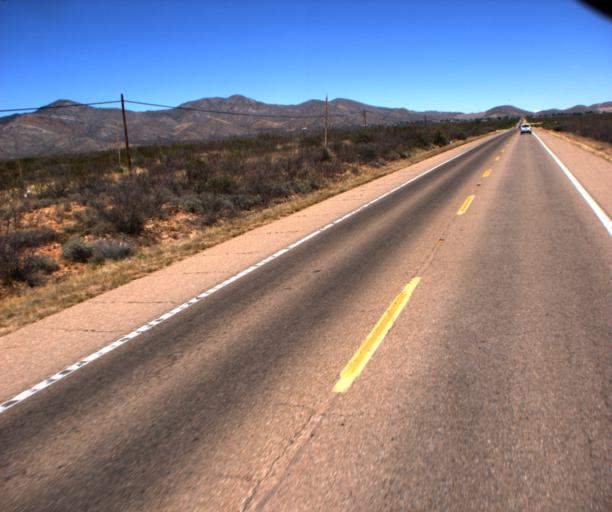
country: US
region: Arizona
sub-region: Cochise County
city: Naco
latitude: 31.3808
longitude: -109.9598
